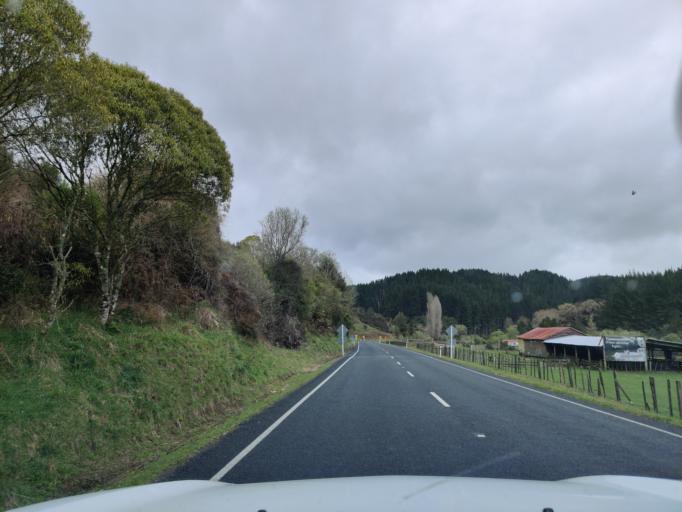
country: NZ
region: Waikato
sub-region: Otorohanga District
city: Otorohanga
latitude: -38.6483
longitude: 175.2131
